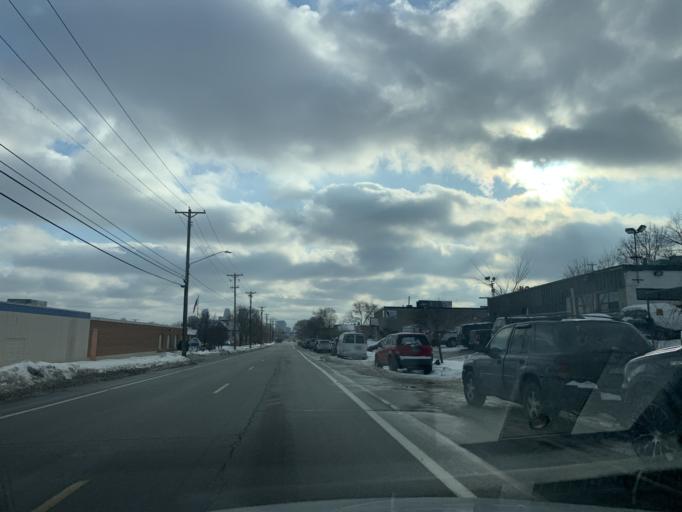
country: US
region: Minnesota
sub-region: Anoka County
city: Columbia Heights
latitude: 45.0160
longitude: -93.2810
